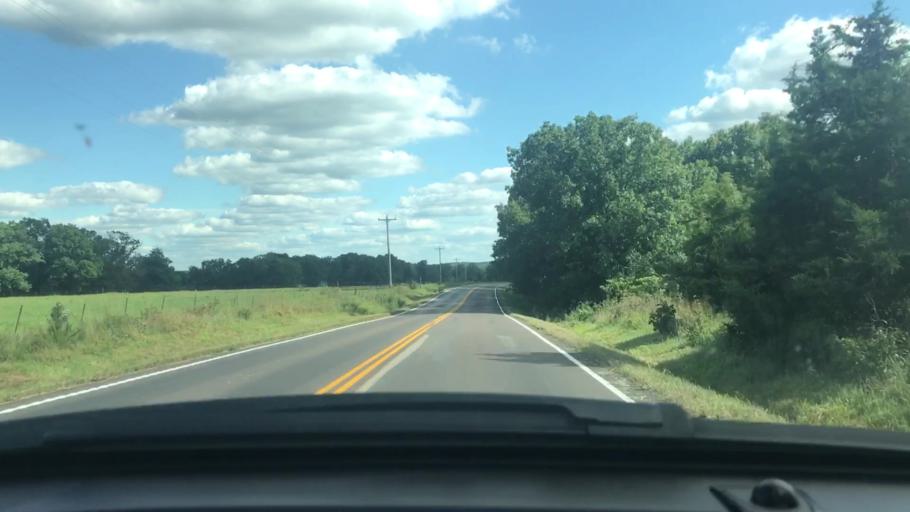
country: US
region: Missouri
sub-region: Wright County
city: Mountain Grove
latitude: 37.2981
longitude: -92.3111
